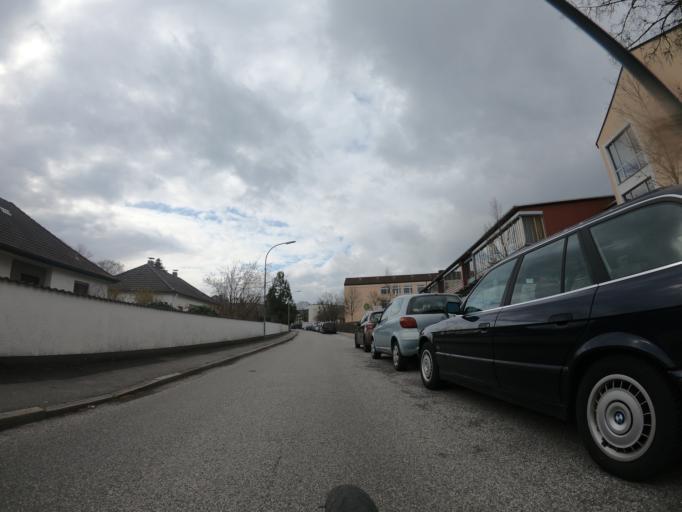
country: DE
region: Bavaria
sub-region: Upper Bavaria
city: Fuerstenfeldbruck
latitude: 48.1693
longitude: 11.2329
